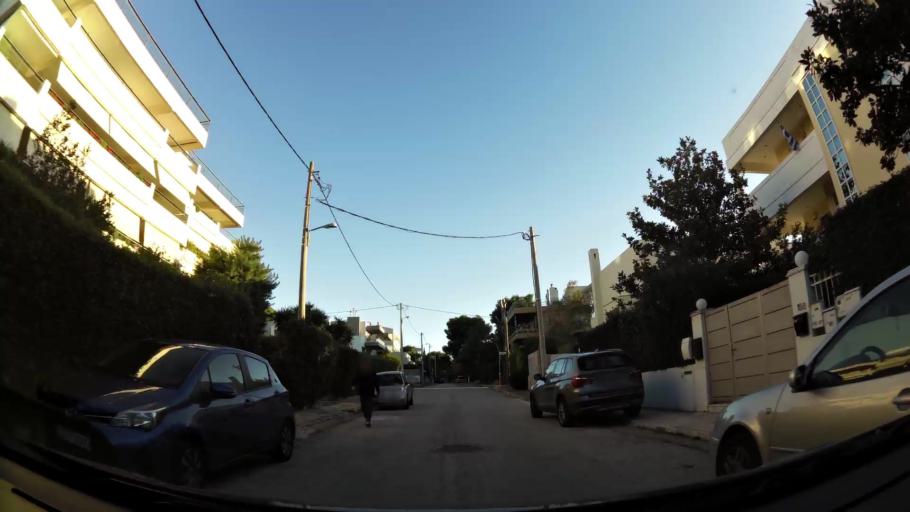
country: GR
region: Attica
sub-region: Nomarchia Athinas
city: Kifisia
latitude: 38.0828
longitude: 23.8240
